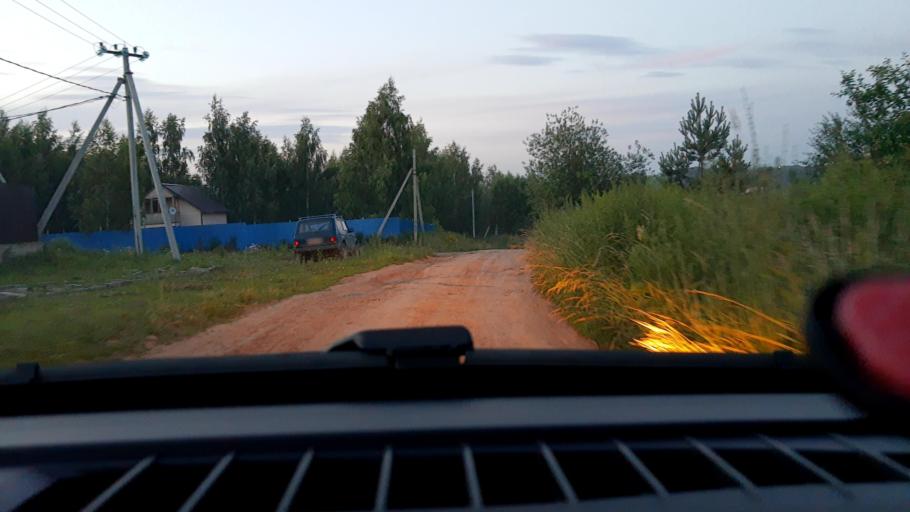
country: RU
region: Nizjnij Novgorod
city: Afonino
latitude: 56.2518
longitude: 44.0670
